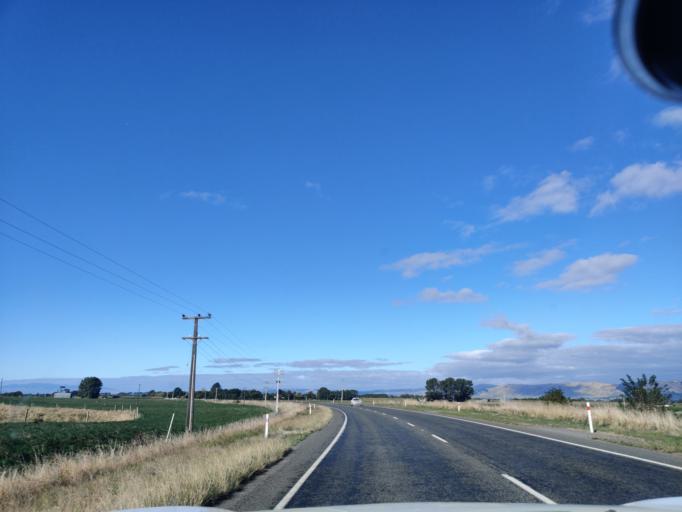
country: NZ
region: Manawatu-Wanganui
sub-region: Horowhenua District
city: Foxton
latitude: -40.4256
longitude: 175.4560
